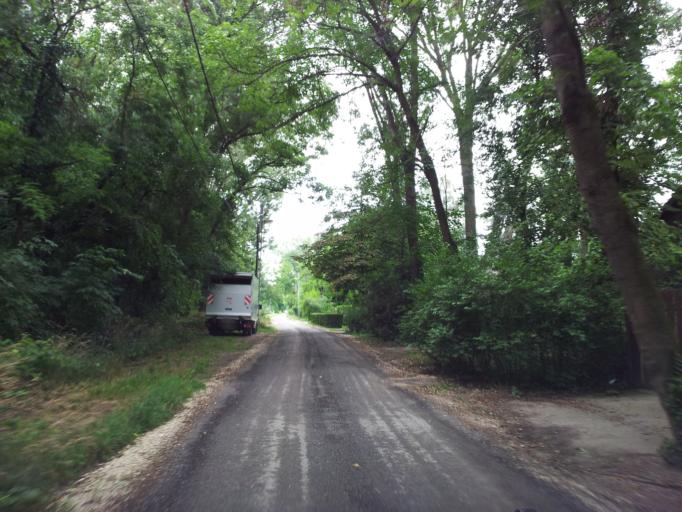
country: HU
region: Pest
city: Szigetujfalu
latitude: 47.2197
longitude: 18.9695
